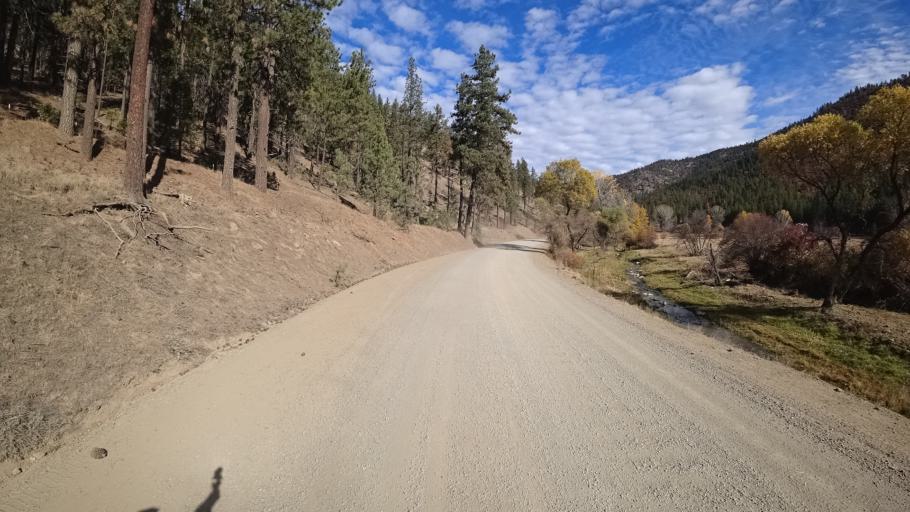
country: US
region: California
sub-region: Siskiyou County
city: Yreka
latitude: 41.6205
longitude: -122.7180
